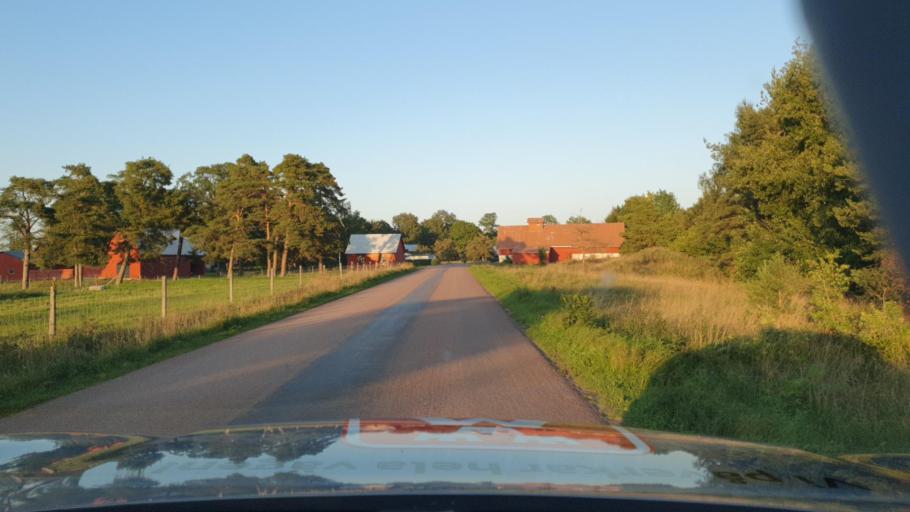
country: SE
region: Gotland
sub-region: Gotland
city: Slite
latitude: 57.6425
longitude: 18.5577
